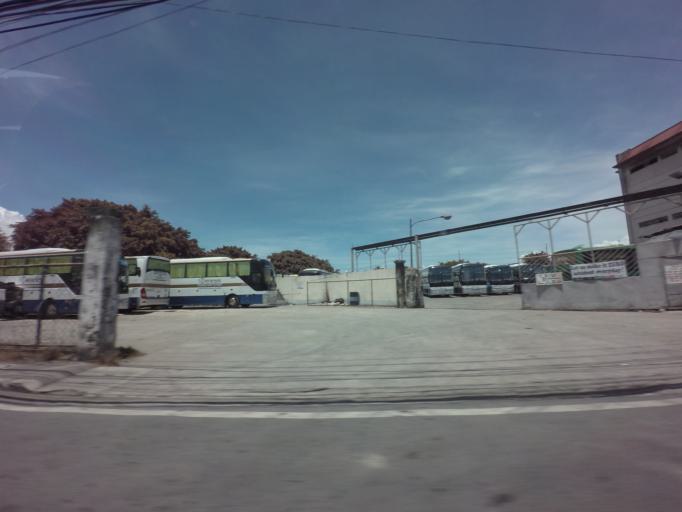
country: PH
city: Sambayanihan People's Village
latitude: 14.4891
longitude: 120.9869
